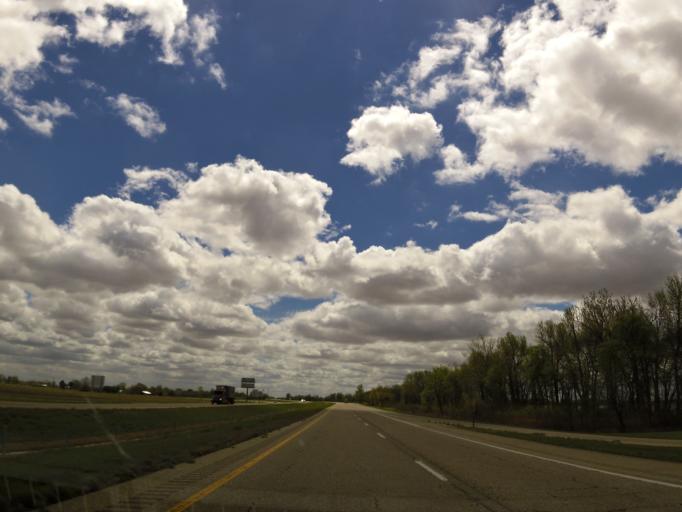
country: US
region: Arkansas
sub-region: Poinsett County
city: Trumann
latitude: 35.6755
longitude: -90.5529
